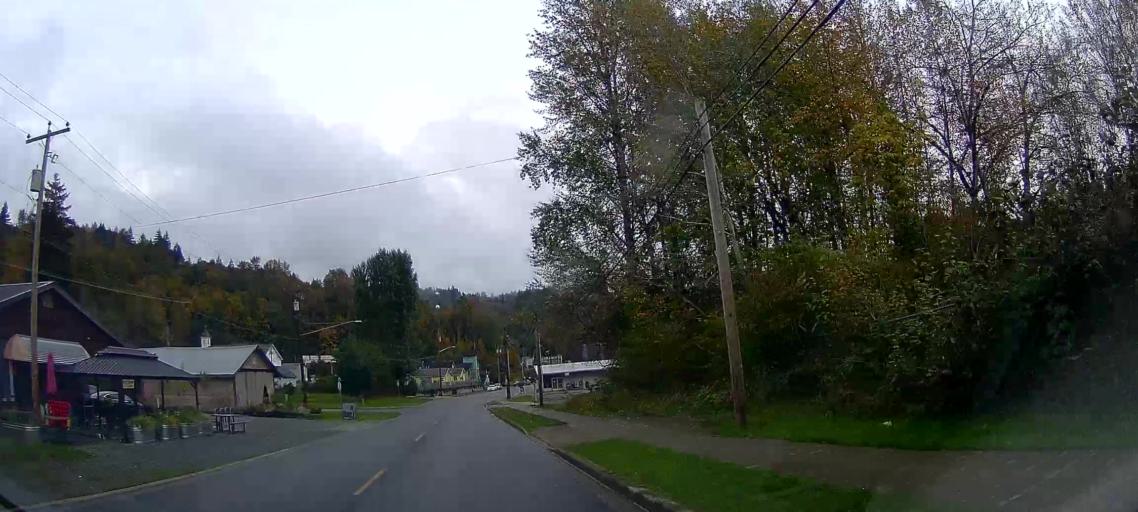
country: US
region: Washington
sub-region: Snohomish County
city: Darrington
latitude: 48.5386
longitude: -121.7533
